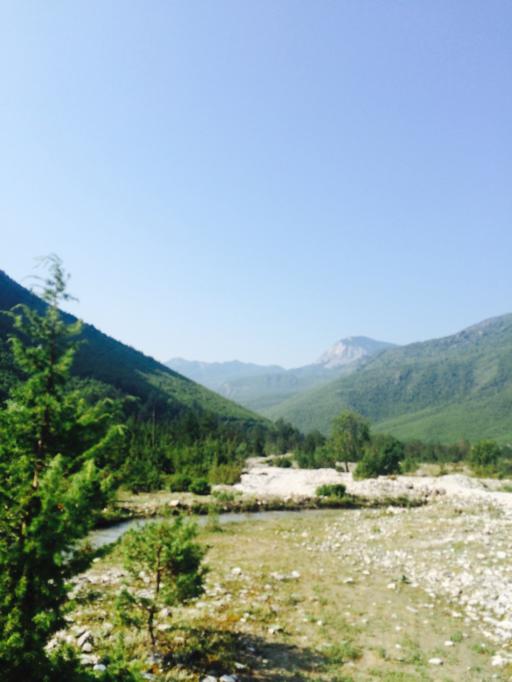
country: AL
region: Shkoder
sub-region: Rrethi i Shkodres
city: Nicaj-Shale
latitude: 42.3560
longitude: 19.7766
